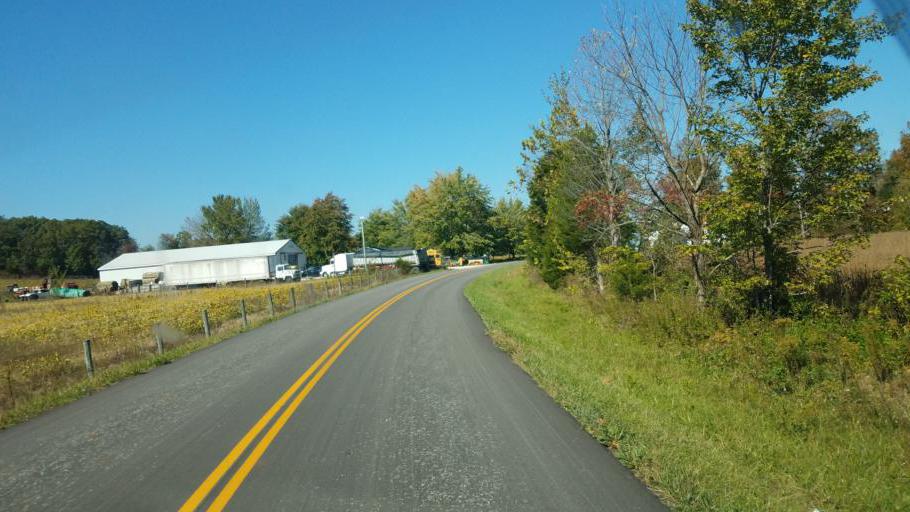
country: US
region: Kentucky
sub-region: Fleming County
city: Flemingsburg
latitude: 38.4481
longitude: -83.5830
